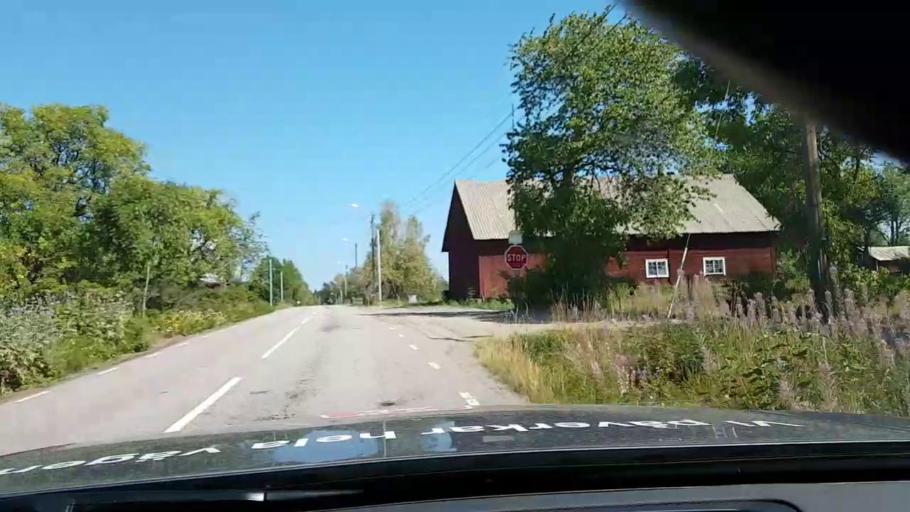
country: SE
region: Kalmar
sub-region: Hultsfreds Kommun
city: Virserum
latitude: 57.1350
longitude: 15.6596
